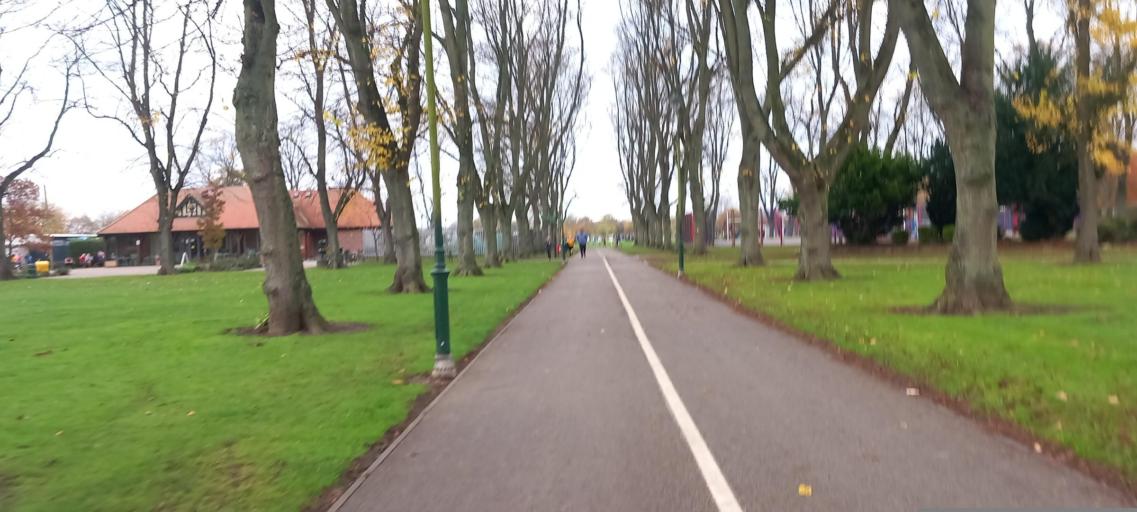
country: GB
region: England
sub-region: East Riding of Yorkshire
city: Airmyn
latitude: 53.7112
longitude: -0.8900
